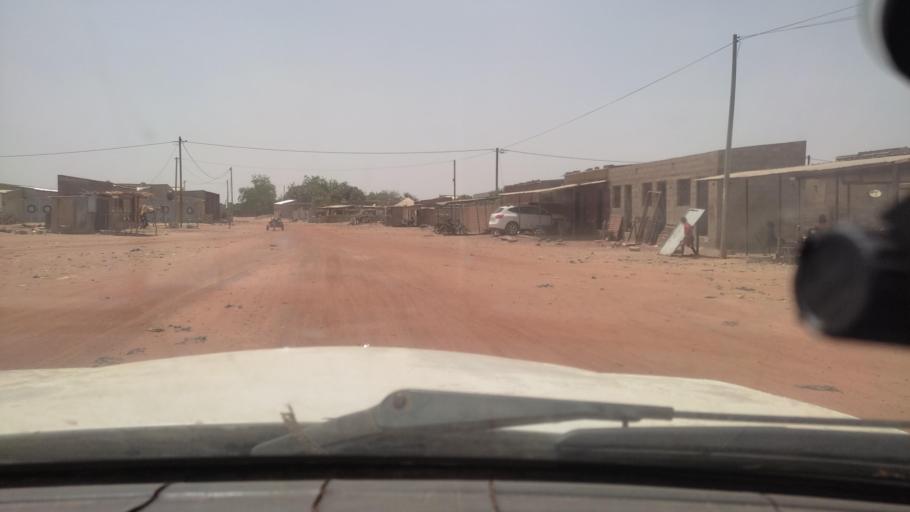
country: BF
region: Est
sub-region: Province du Gourma
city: Fada N'gourma
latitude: 12.0732
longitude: 0.3630
